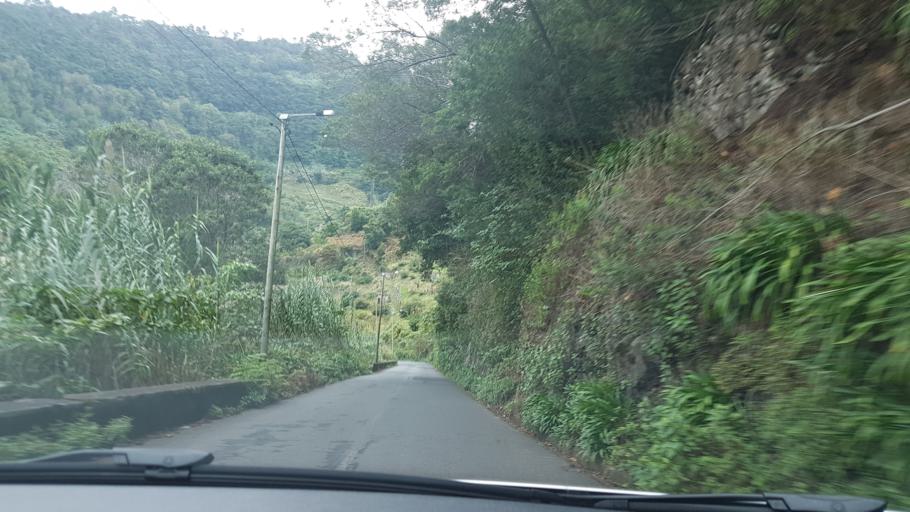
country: PT
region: Madeira
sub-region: Santana
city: Santana
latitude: 32.8199
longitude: -16.9008
